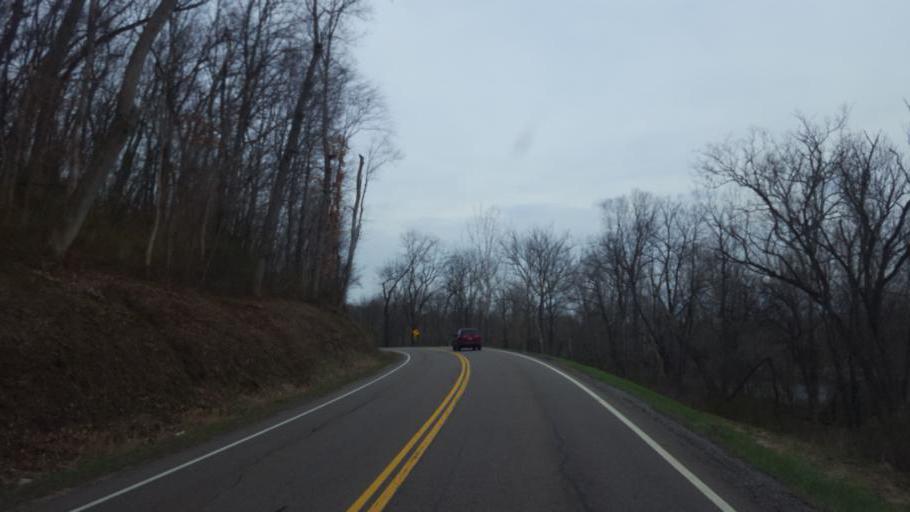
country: US
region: Ohio
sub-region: Knox County
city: Danville
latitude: 40.4059
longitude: -82.3068
